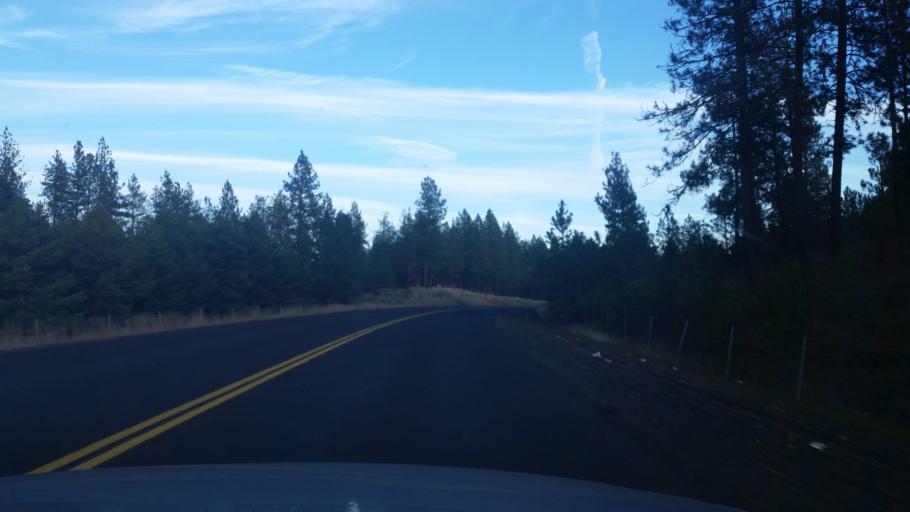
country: US
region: Washington
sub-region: Spokane County
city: Cheney
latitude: 47.4779
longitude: -117.5323
